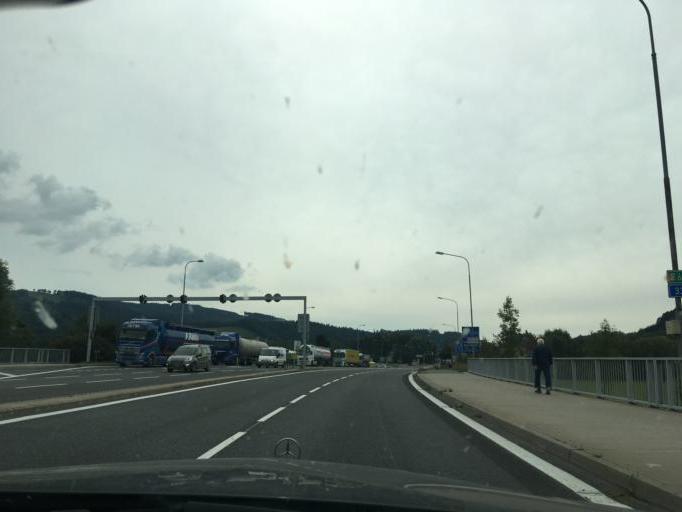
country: CZ
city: Velke Porici
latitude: 50.4295
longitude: 16.1971
